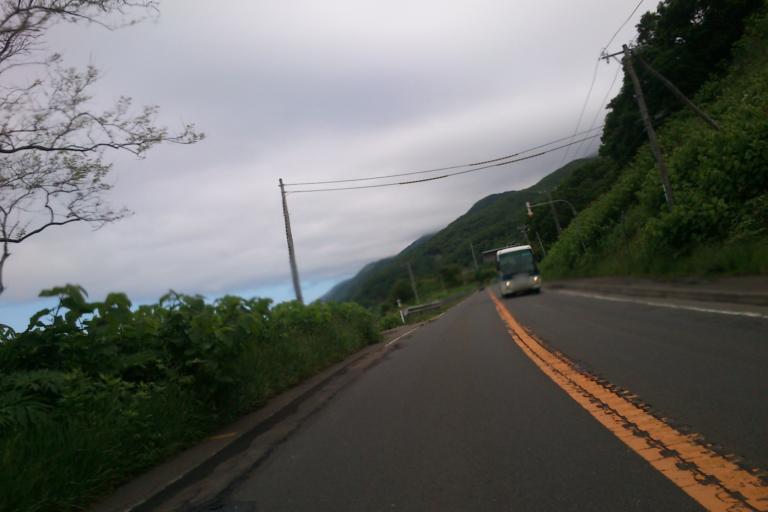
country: JP
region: Hokkaido
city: Ishikari
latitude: 43.4154
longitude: 141.4305
